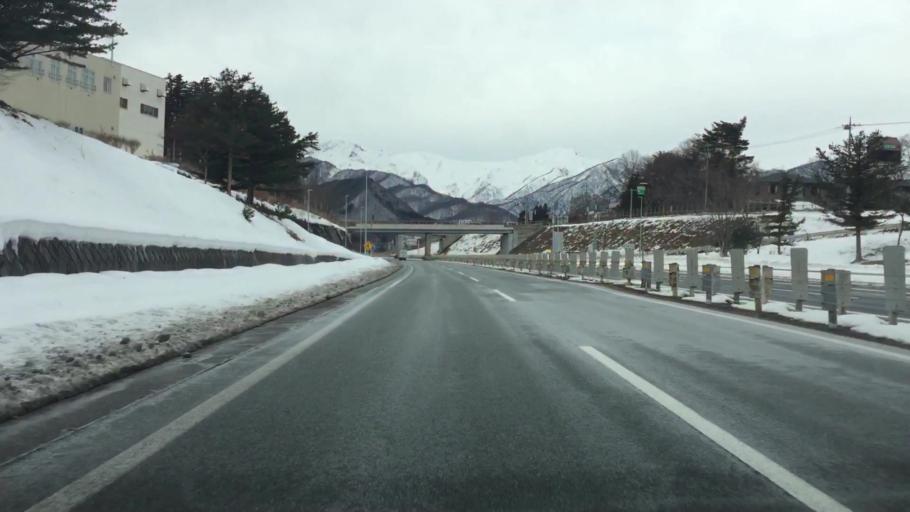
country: JP
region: Gunma
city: Numata
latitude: 36.7471
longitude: 138.9754
